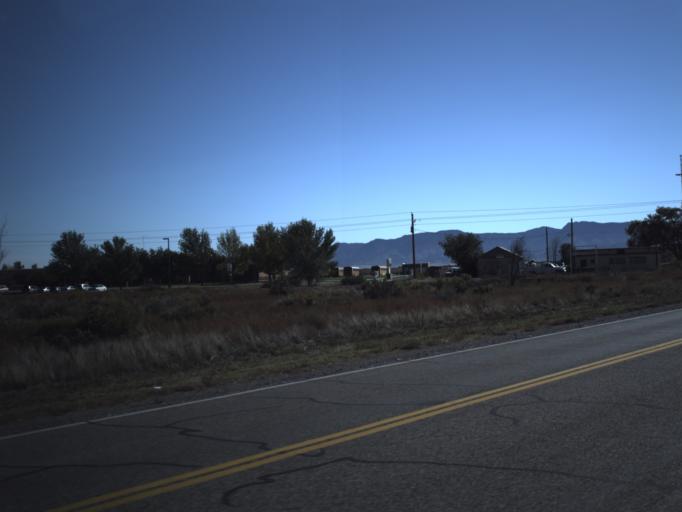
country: US
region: Utah
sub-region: Washington County
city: Enterprise
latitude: 37.7099
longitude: -113.6576
